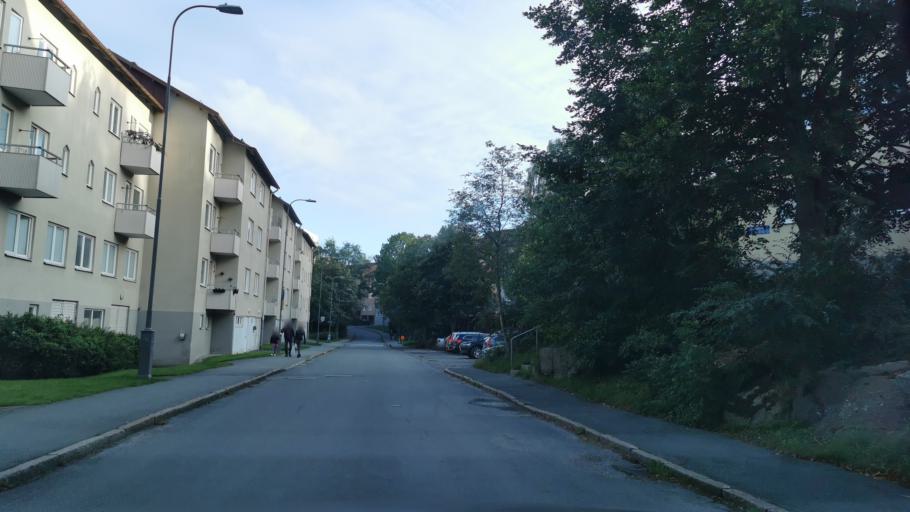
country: SE
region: Vaestra Goetaland
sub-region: Goteborg
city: Majorna
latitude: 57.6707
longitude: 11.9235
